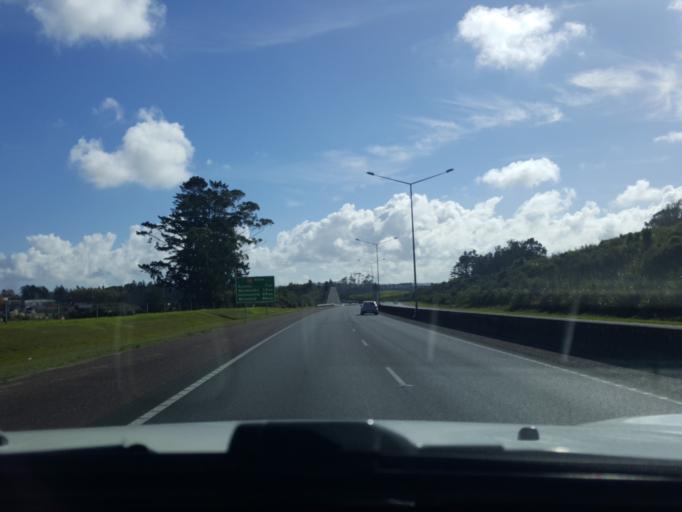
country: NZ
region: Auckland
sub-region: Auckland
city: Rosebank
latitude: -36.8113
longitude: 174.6103
